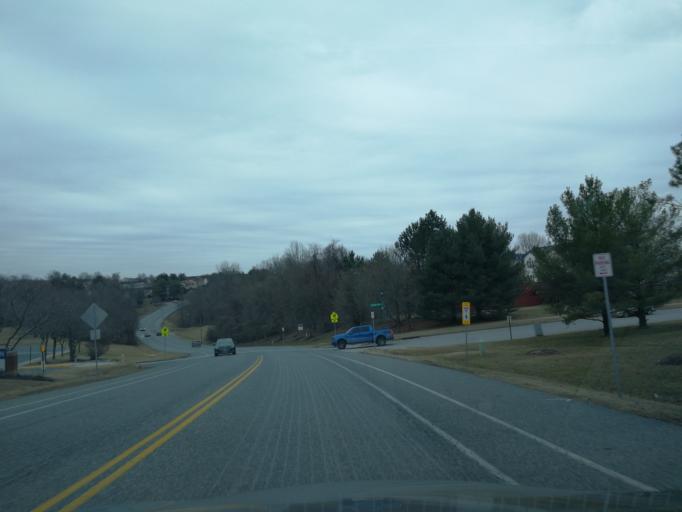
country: US
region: Maryland
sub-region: Harford County
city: Bel Air South
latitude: 39.4775
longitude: -76.3271
